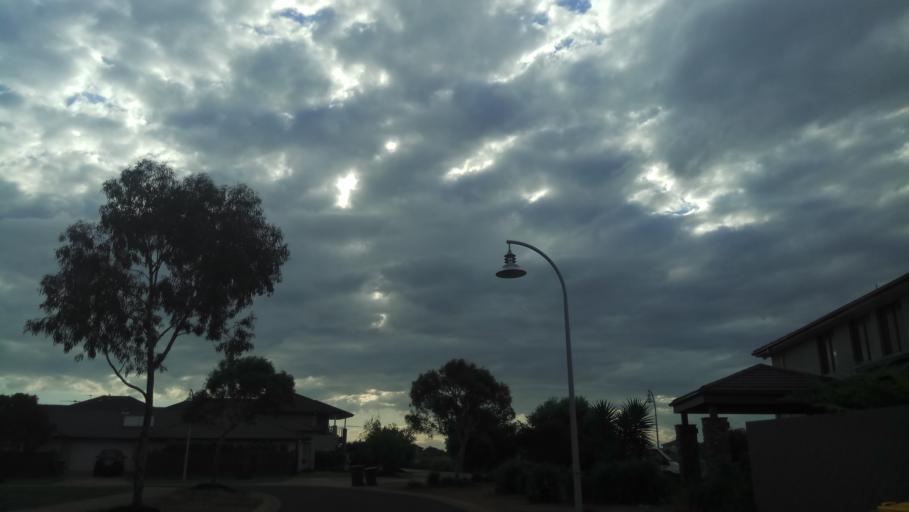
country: AU
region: Victoria
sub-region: Hobsons Bay
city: Altona Meadows
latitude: -37.8970
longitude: 144.7735
